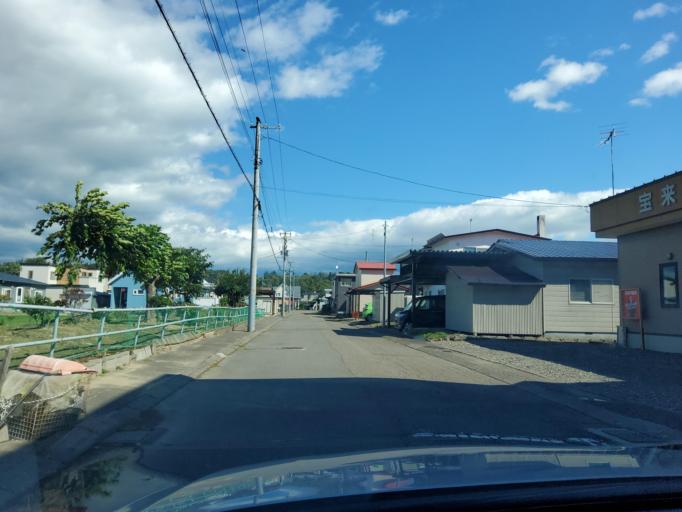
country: JP
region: Hokkaido
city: Obihiro
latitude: 42.9496
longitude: 143.2157
